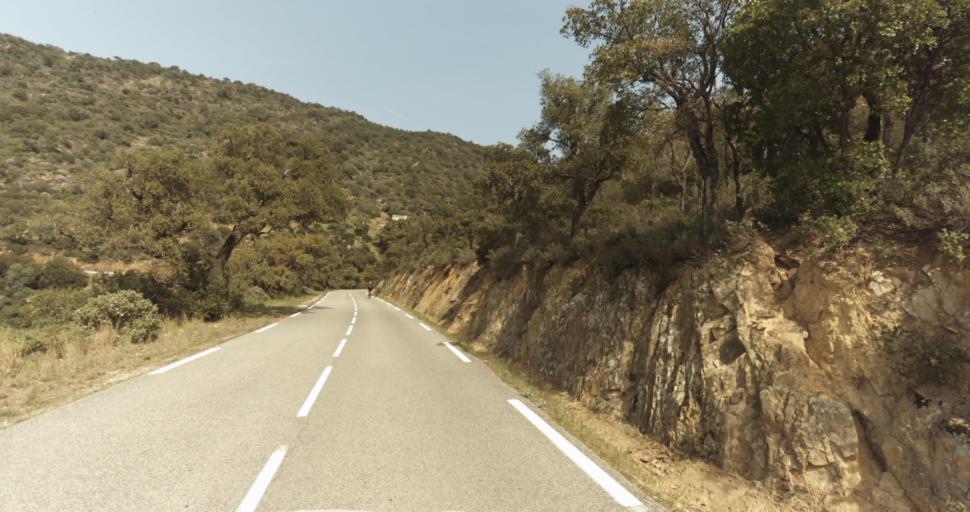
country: FR
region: Provence-Alpes-Cote d'Azur
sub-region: Departement du Var
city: Bormes-les-Mimosas
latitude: 43.1621
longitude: 6.3435
